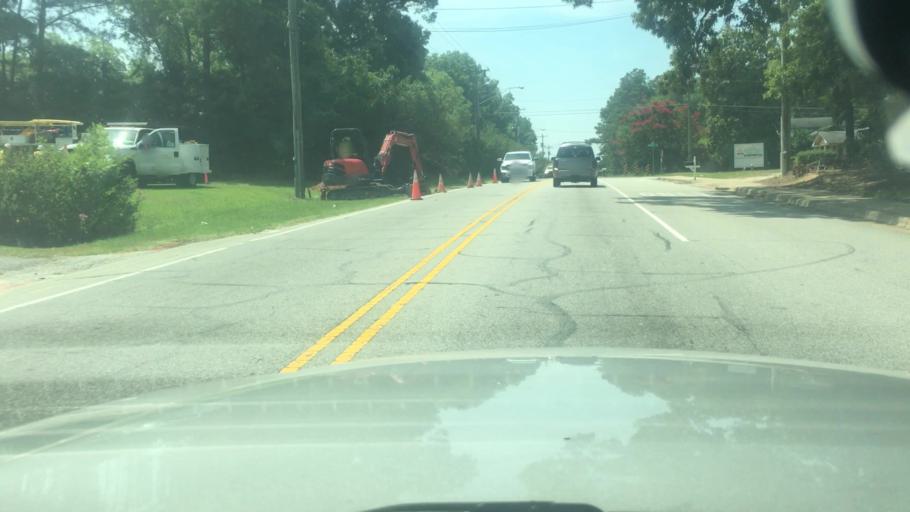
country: US
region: North Carolina
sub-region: Hoke County
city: Rockfish
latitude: 35.0387
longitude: -78.9973
